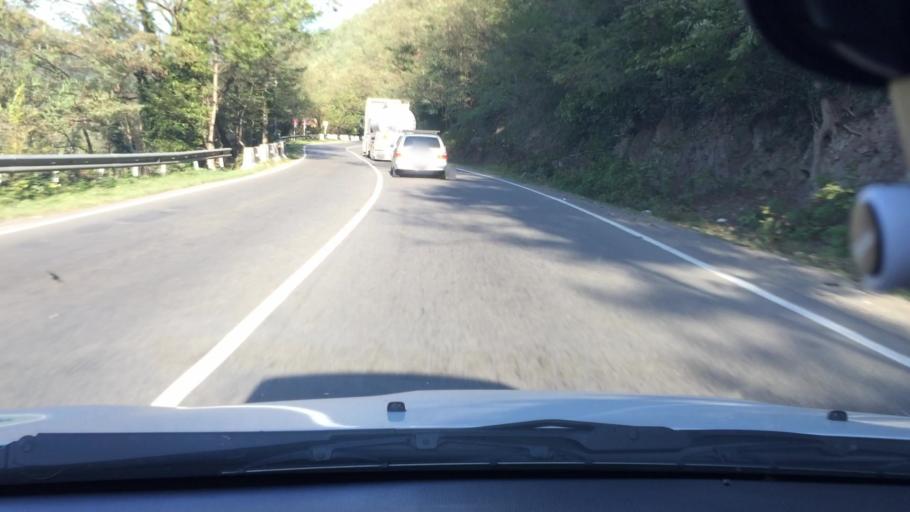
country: GE
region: Imereti
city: Kharagauli
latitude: 42.1000
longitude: 43.2292
